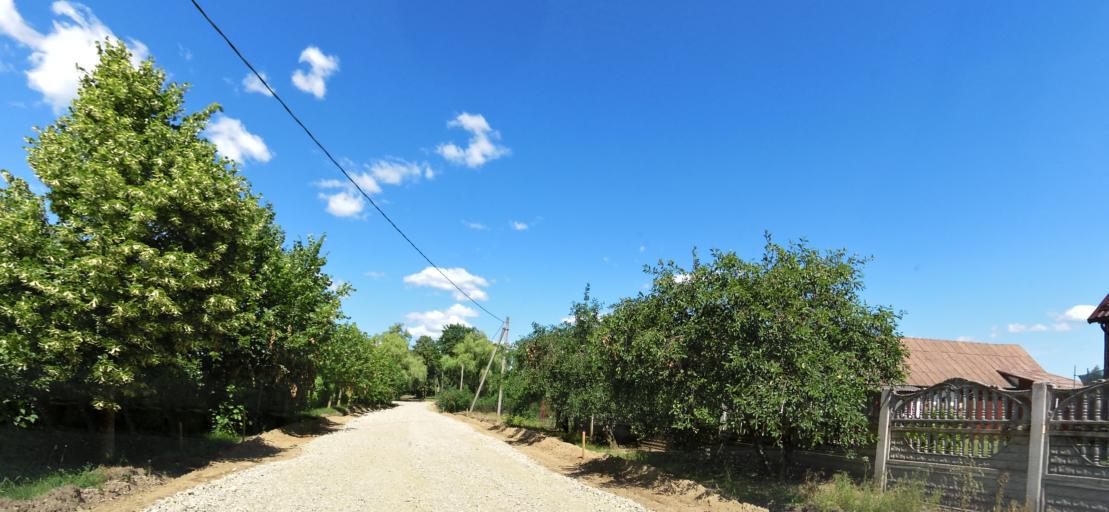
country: LT
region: Panevezys
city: Pasvalys
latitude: 56.2285
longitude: 24.4177
